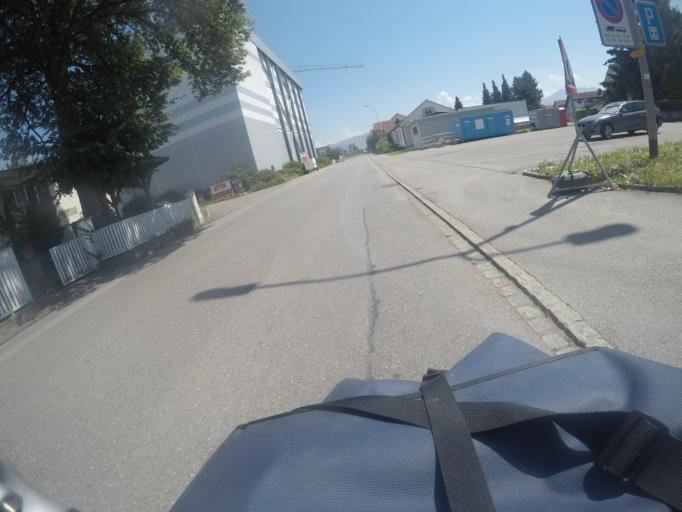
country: CH
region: Saint Gallen
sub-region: Wahlkreis Rheintal
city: Sankt Margrethen
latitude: 47.4518
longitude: 9.6394
